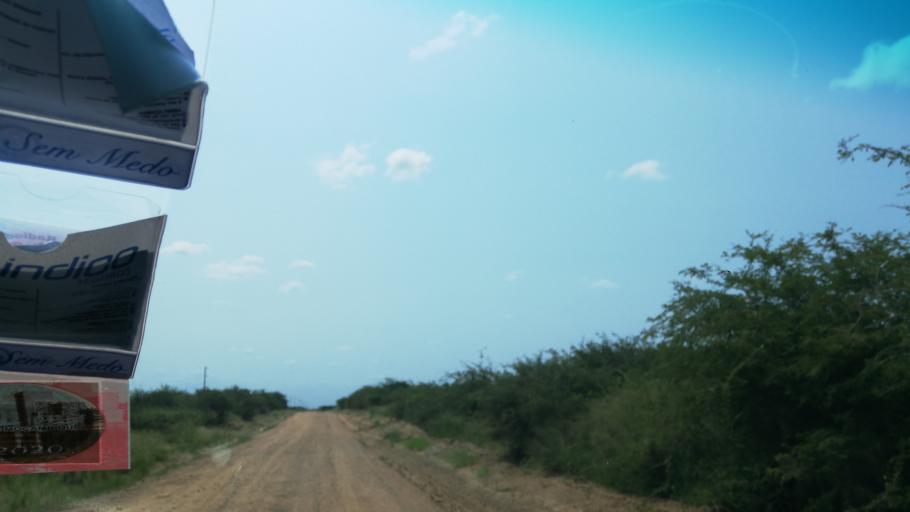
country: MZ
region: Maputo
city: Matola
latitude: -26.0792
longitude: 32.3911
